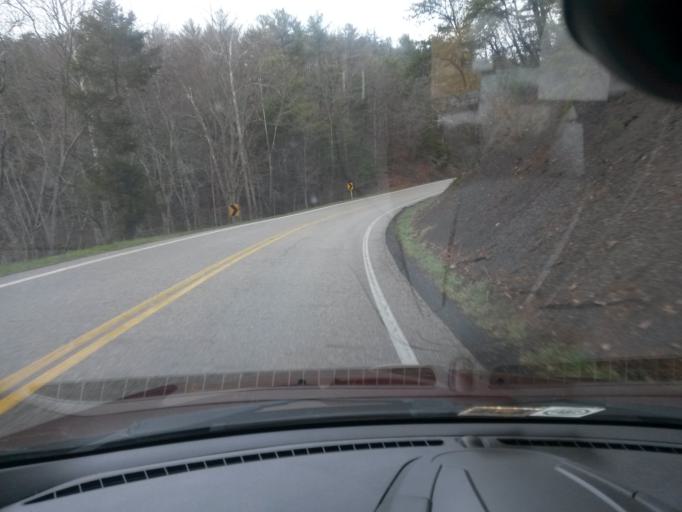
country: US
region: Virginia
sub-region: Alleghany County
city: Clifton Forge
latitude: 37.9042
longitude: -79.7405
